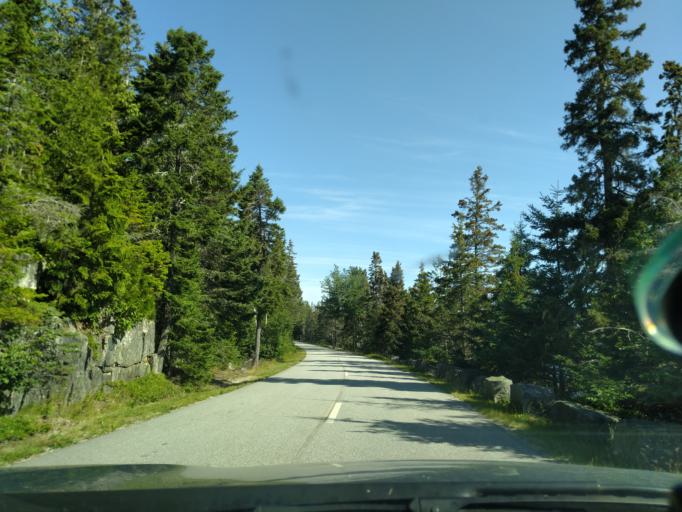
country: US
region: Maine
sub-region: Hancock County
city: Gouldsboro
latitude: 44.3422
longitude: -68.0442
